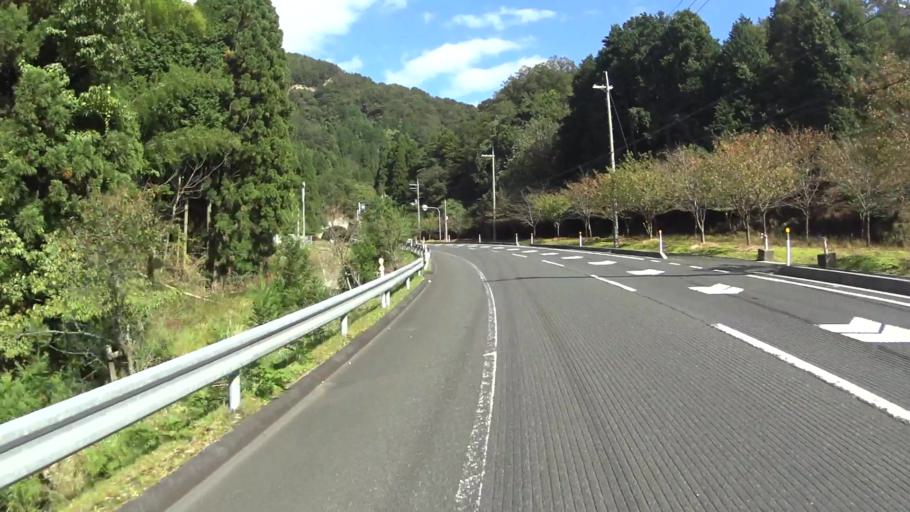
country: JP
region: Hyogo
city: Toyooka
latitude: 35.5755
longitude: 134.9947
